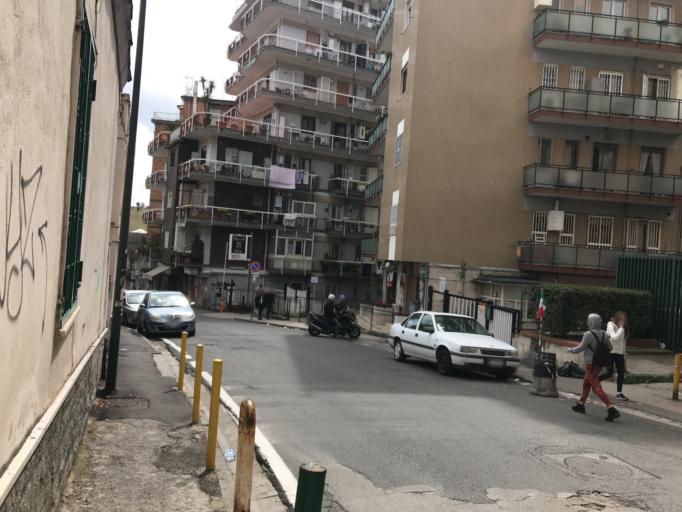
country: IT
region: Campania
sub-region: Provincia di Napoli
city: Napoli
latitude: 40.8554
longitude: 14.2232
